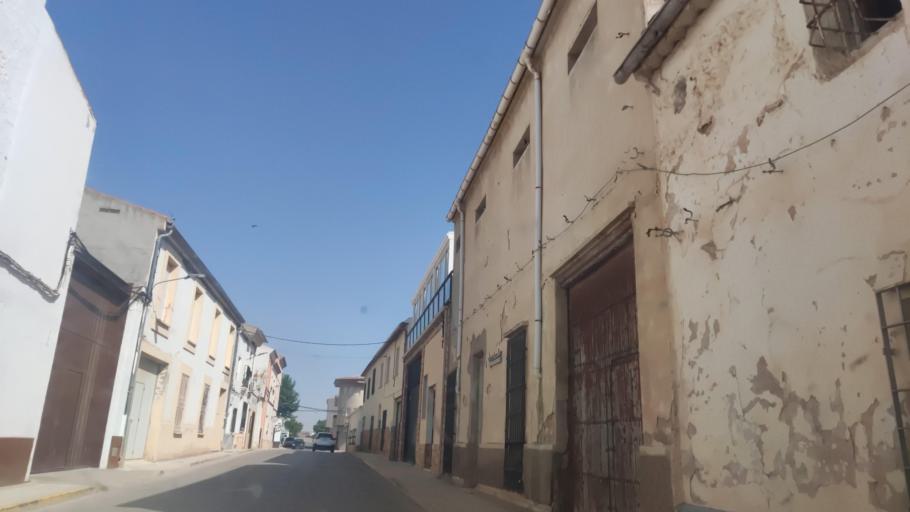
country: ES
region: Castille-La Mancha
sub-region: Provincia de Albacete
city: La Gineta
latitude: 39.1145
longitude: -1.9974
